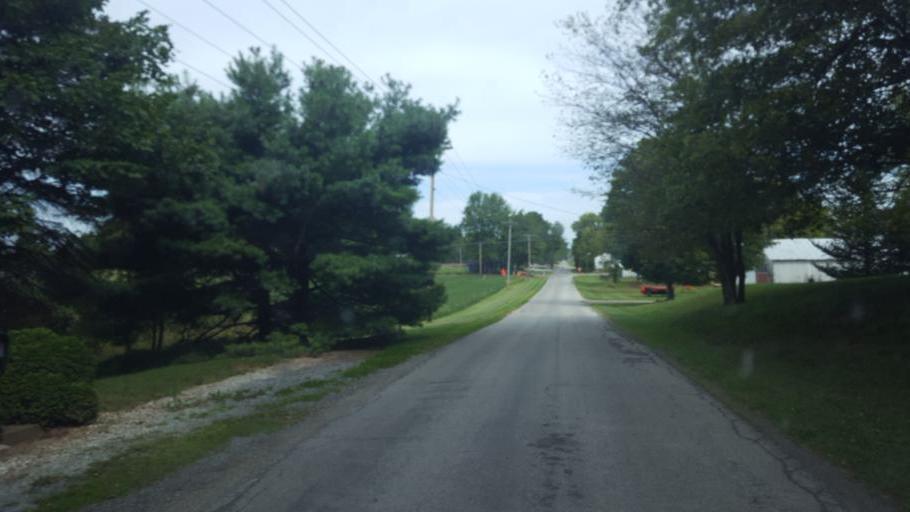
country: US
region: Ohio
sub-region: Knox County
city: Centerburg
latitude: 40.3622
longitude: -82.7248
